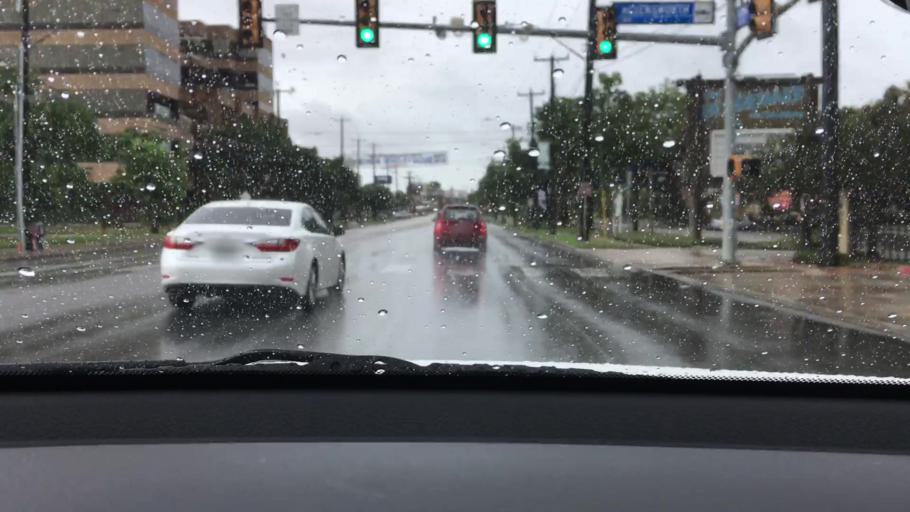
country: US
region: Texas
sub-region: Bexar County
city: Terrell Hills
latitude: 29.4642
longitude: -98.4648
